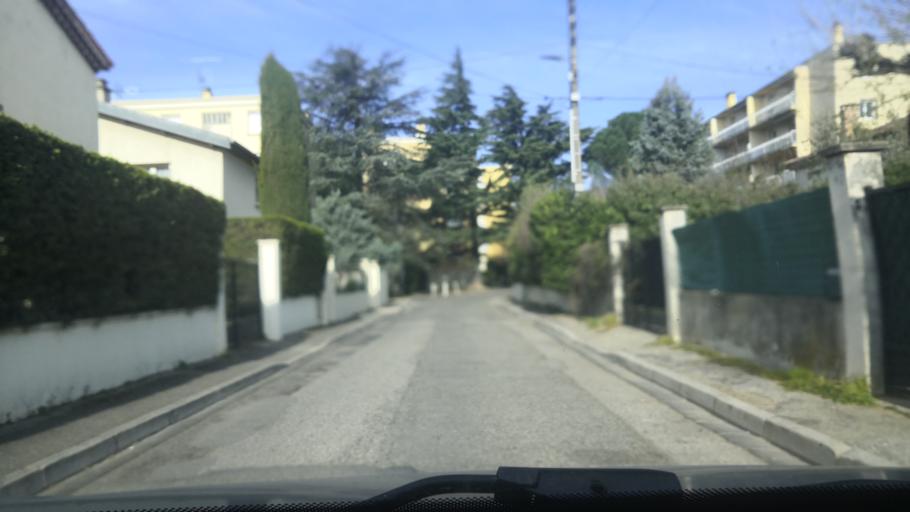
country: FR
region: Rhone-Alpes
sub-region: Departement de la Drome
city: Montelimar
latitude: 44.5455
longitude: 4.7433
